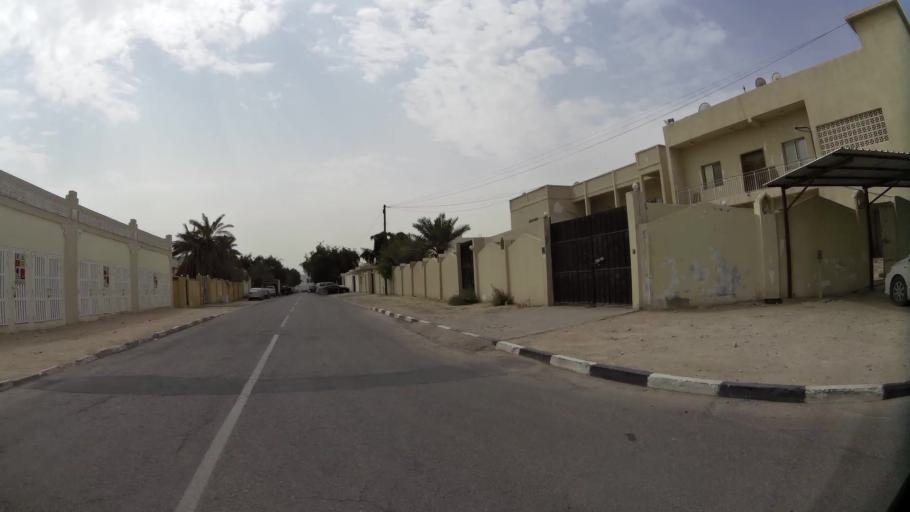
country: QA
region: Baladiyat ad Dawhah
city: Doha
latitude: 25.3062
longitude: 51.4919
